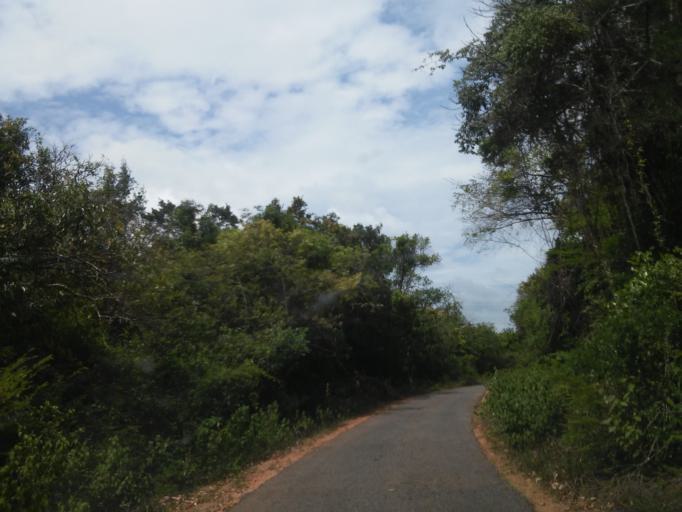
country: LK
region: Central
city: Sigiriya
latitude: 8.0891
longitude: 80.6814
